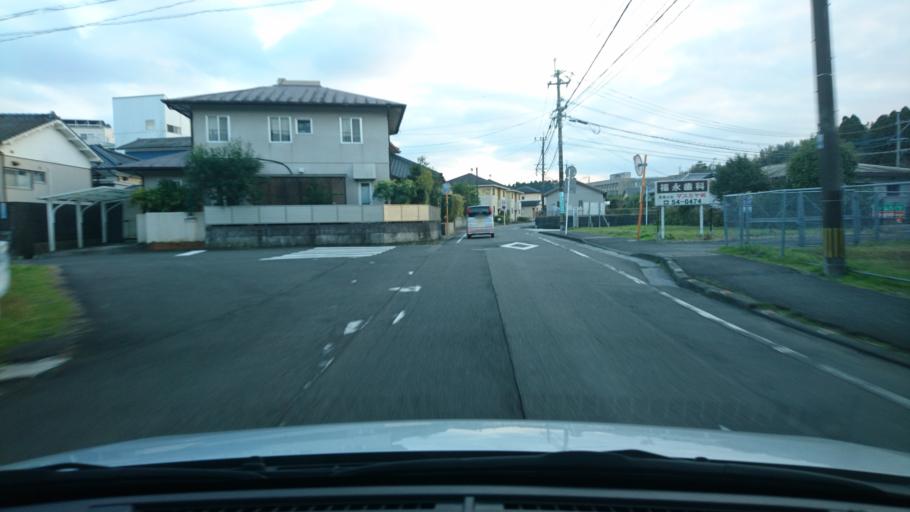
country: JP
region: Miyazaki
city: Miyazaki-shi
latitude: 31.8677
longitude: 131.4276
